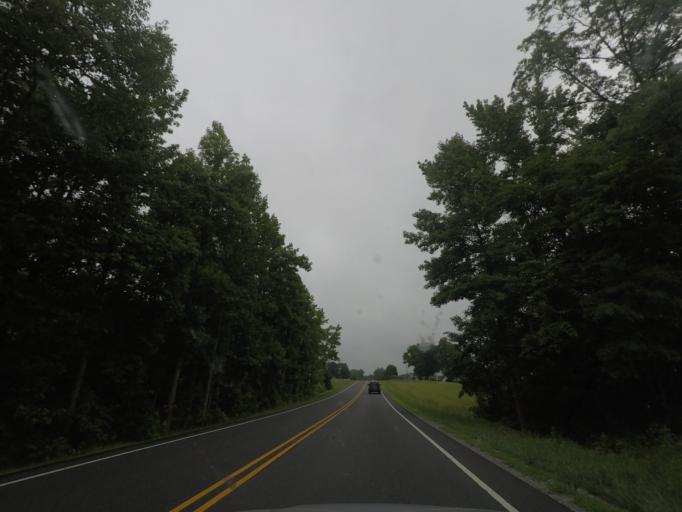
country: US
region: Virginia
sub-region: Prince Edward County
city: Hampden Sydney
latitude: 37.1279
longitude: -78.4504
